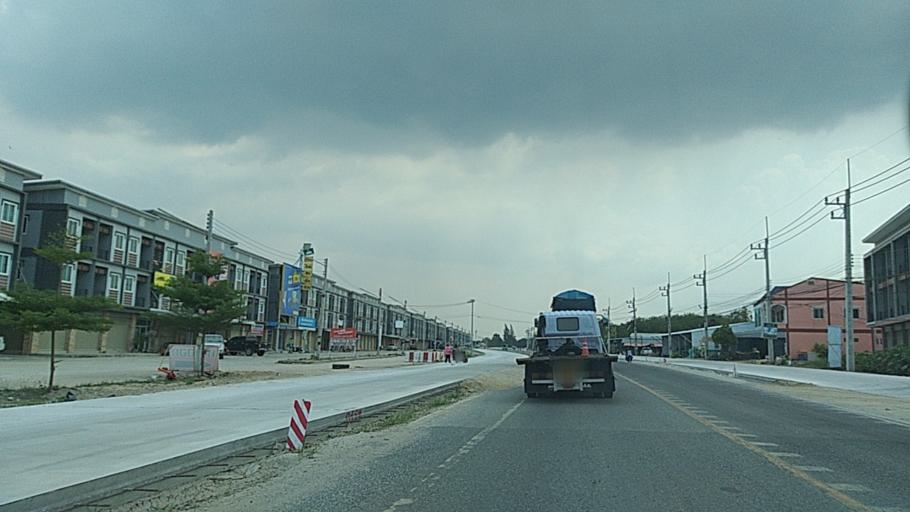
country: TH
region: Chon Buri
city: Ban Bueng
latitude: 13.3228
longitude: 101.1855
